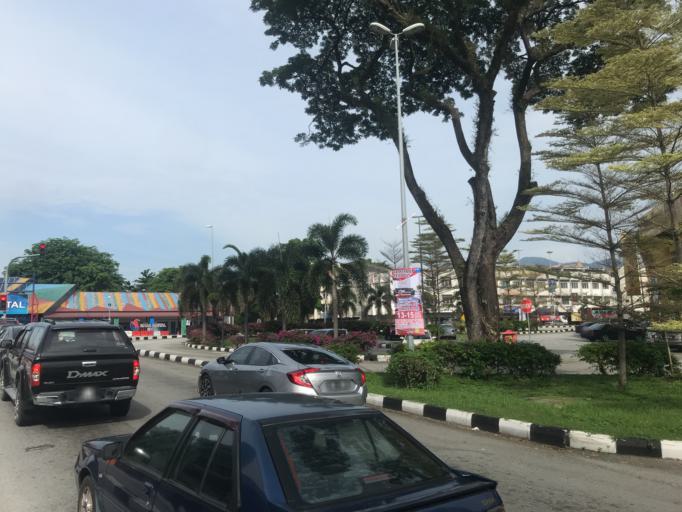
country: MY
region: Perak
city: Ipoh
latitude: 4.5917
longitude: 101.0758
